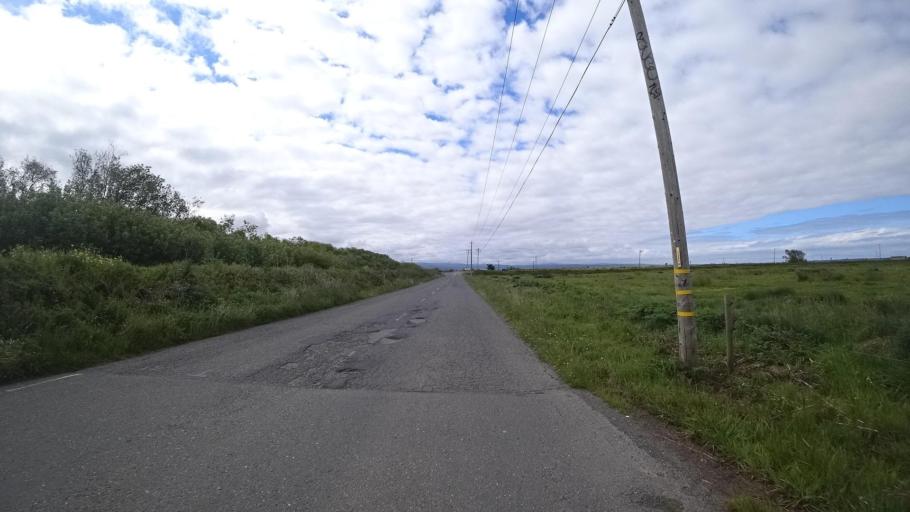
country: US
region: California
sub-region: Humboldt County
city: Arcata
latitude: 40.8701
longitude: -124.1059
